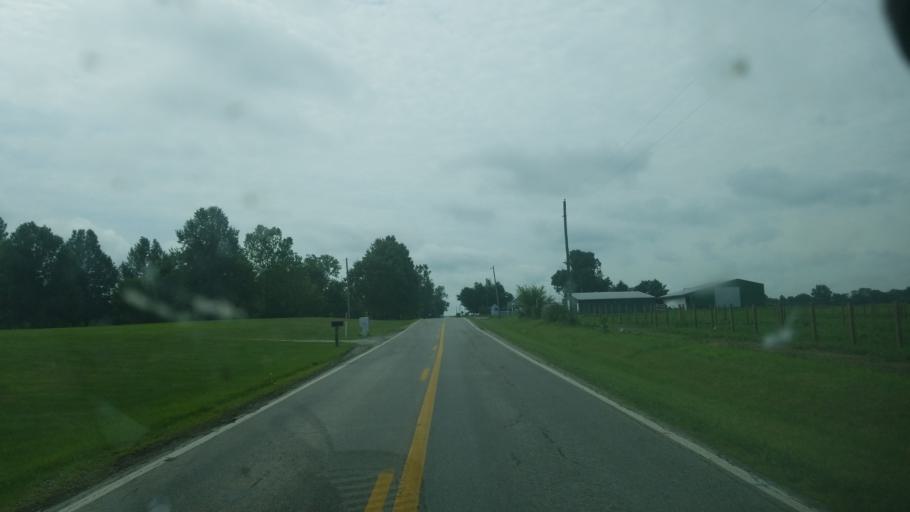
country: US
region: Ohio
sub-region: Licking County
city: Johnstown
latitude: 40.1420
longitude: -82.7606
